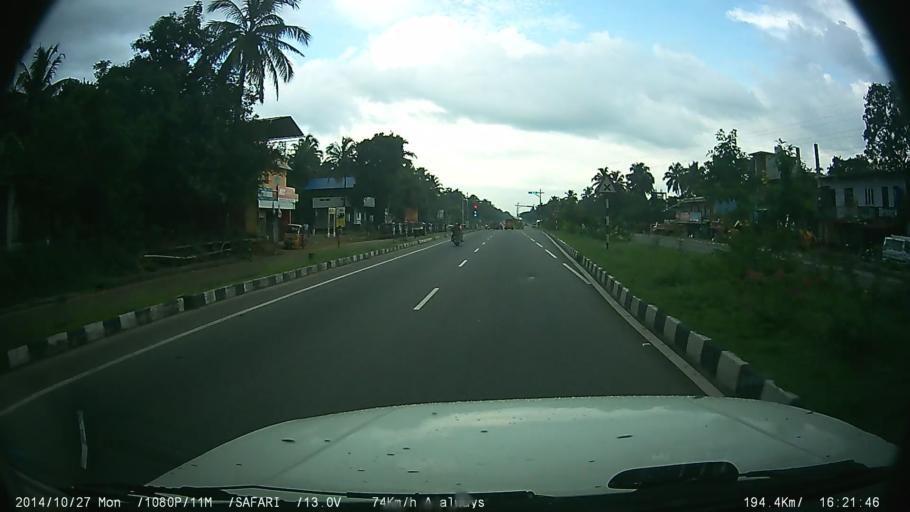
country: IN
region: Kerala
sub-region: Thrissur District
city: Trichur
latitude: 10.4672
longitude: 76.2577
